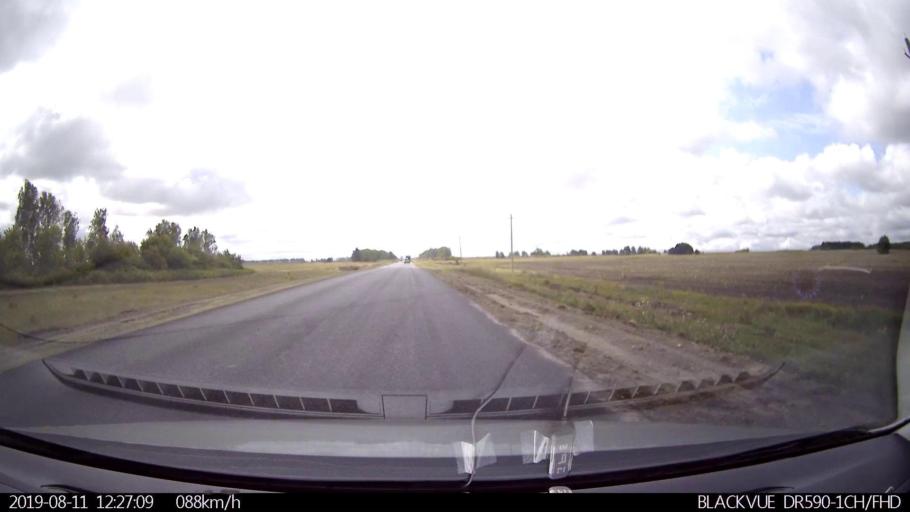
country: RU
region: Ulyanovsk
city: Ignatovka
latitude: 53.8573
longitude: 47.9241
